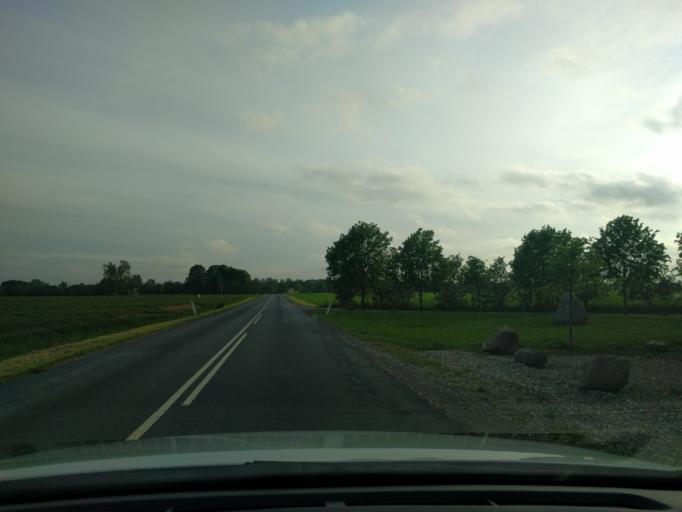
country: DK
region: South Denmark
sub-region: Kerteminde Kommune
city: Kerteminde
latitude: 55.4190
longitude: 10.6096
